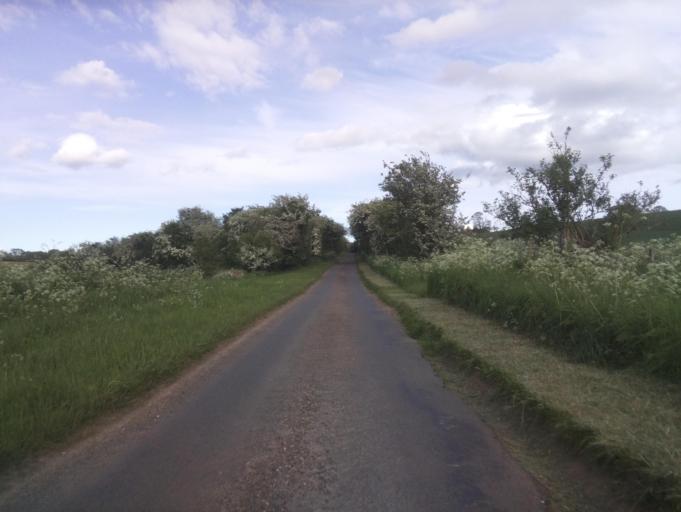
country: GB
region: England
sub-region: Gloucestershire
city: Shipton Village
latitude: 51.8776
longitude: -1.9393
